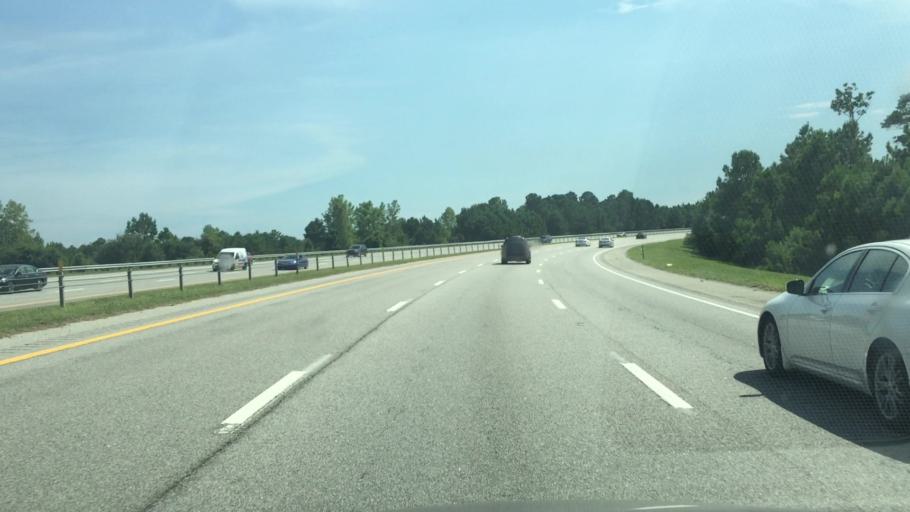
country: US
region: South Carolina
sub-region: Horry County
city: Myrtle Beach
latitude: 33.7844
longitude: -78.8048
